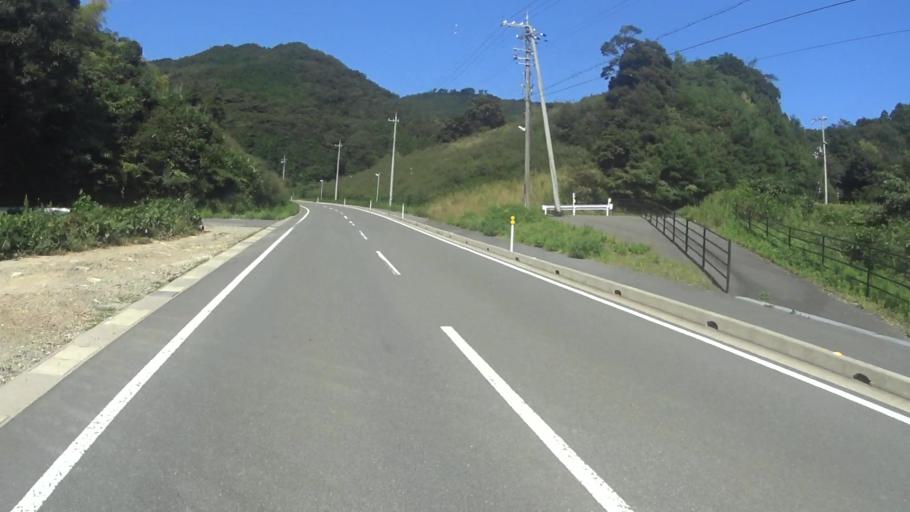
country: JP
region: Kyoto
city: Miyazu
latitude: 35.6840
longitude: 135.2894
